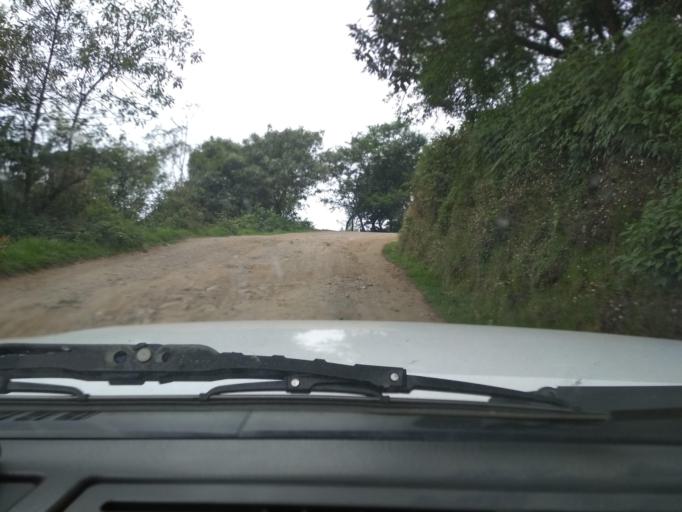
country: MX
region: Veracruz
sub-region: La Perla
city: Chilapa
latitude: 18.9985
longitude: -97.1690
